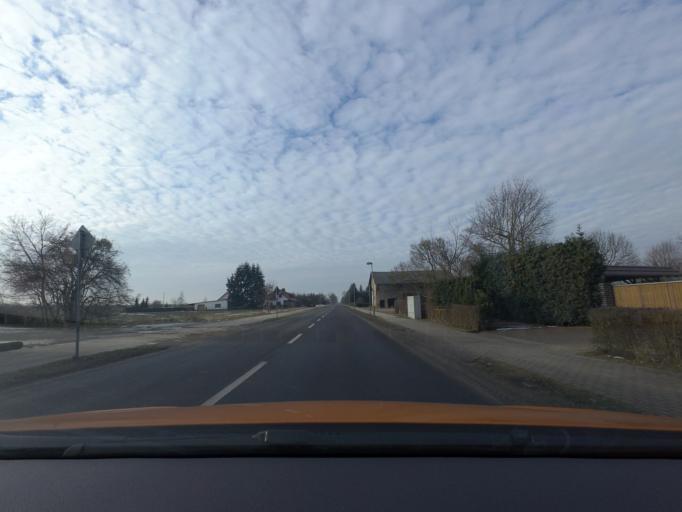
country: DE
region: Brandenburg
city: Gransee
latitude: 52.8988
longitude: 13.1879
